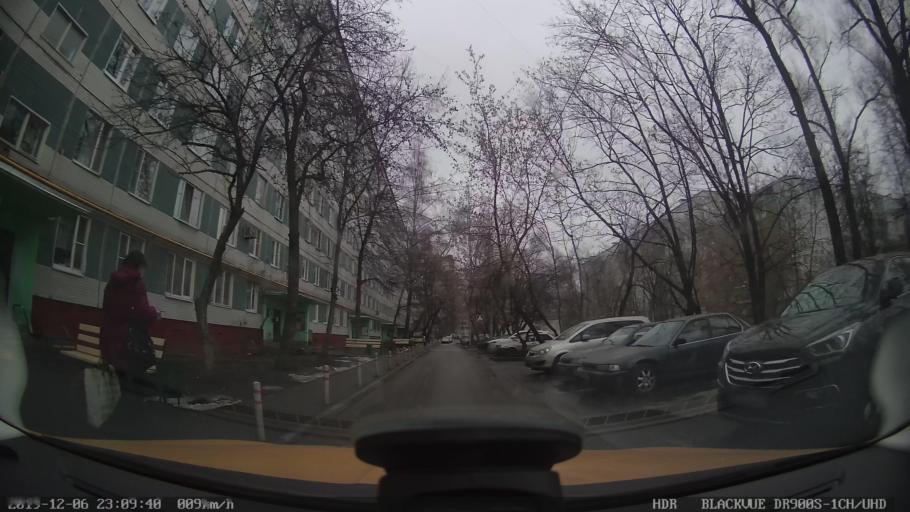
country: RU
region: Moskovskaya
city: Vostochnoe Degunino
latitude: 55.8695
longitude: 37.5644
